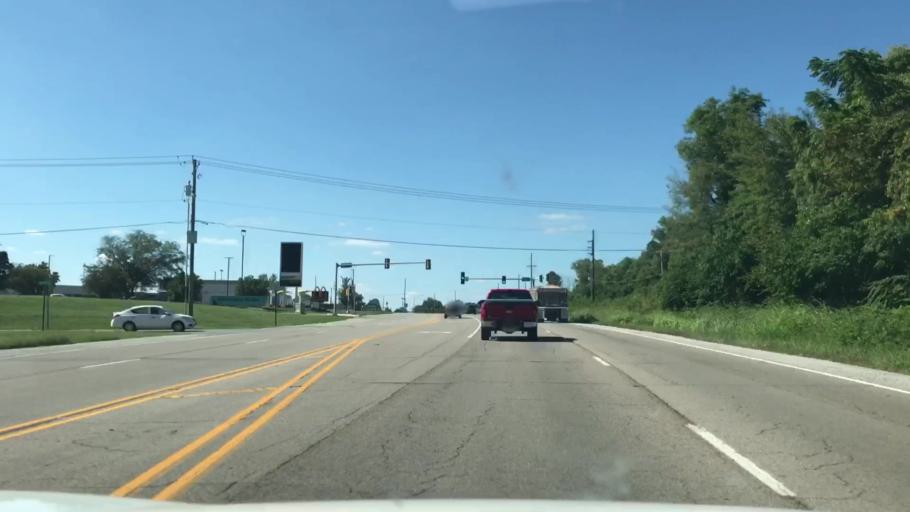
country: US
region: Illinois
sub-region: Saint Clair County
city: Swansea
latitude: 38.5440
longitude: -90.0499
